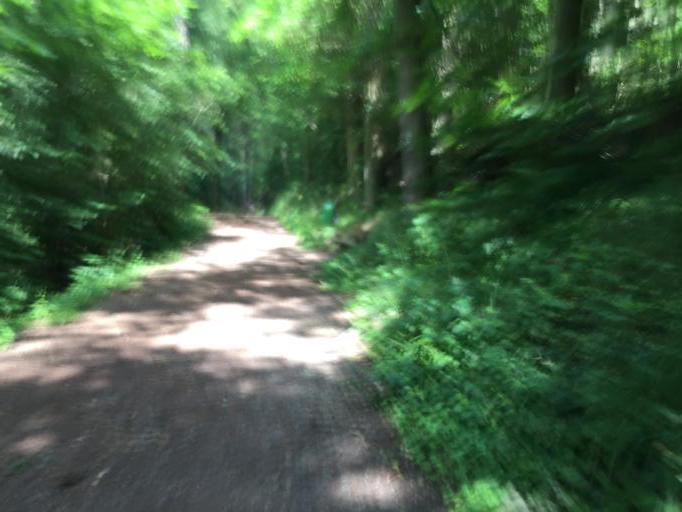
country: DE
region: Rheinland-Pfalz
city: Holler
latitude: 50.4308
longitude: 7.8467
